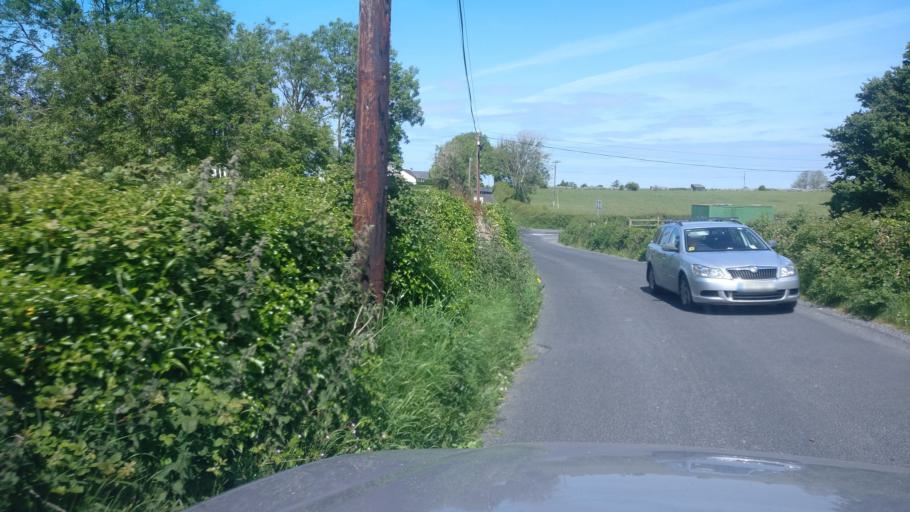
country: IE
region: Connaught
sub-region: County Galway
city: Gort
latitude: 53.0852
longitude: -8.8005
